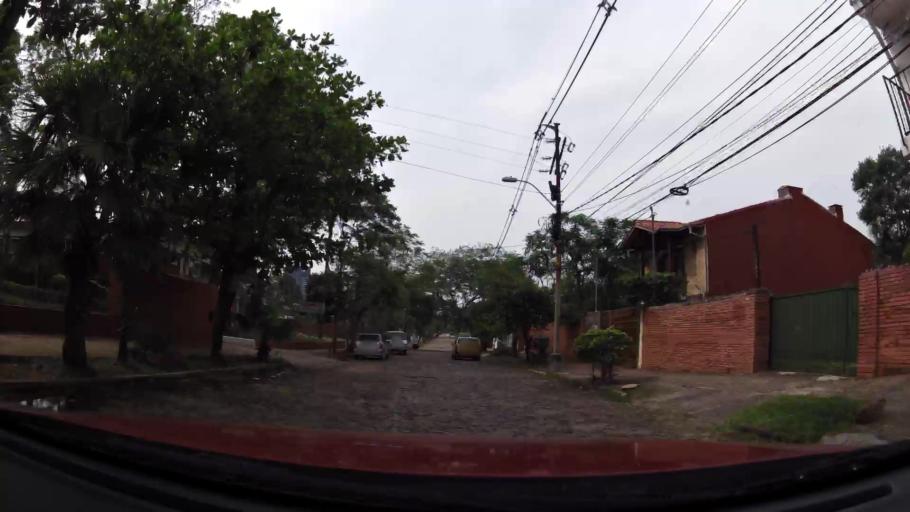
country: PY
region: Central
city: Fernando de la Mora
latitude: -25.2922
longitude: -57.5615
